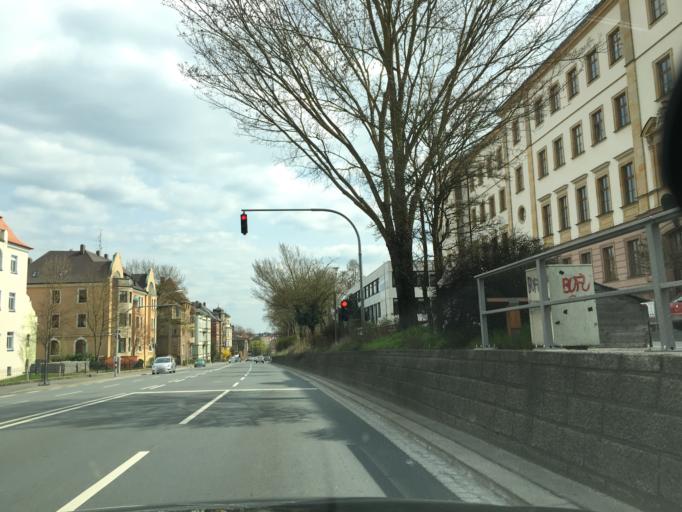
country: DE
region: Bavaria
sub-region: Upper Palatinate
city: Amberg
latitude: 49.4430
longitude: 11.8505
